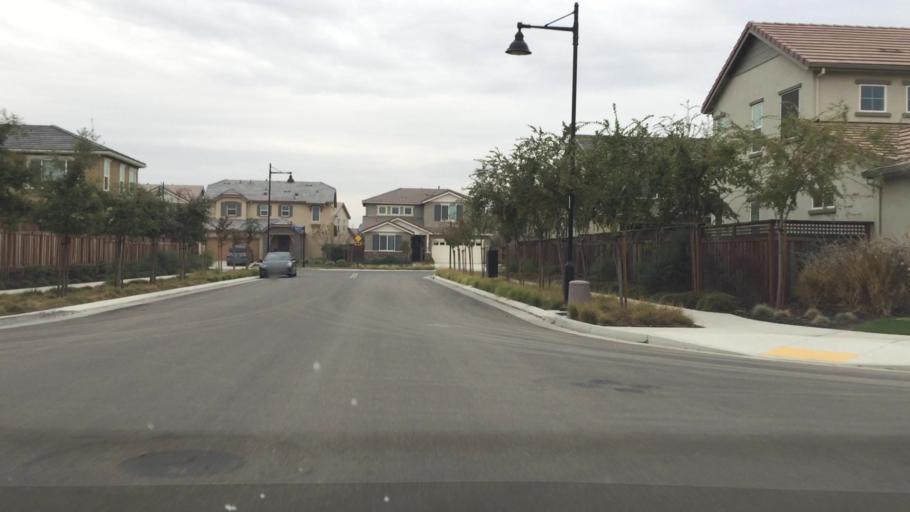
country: US
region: California
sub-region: San Joaquin County
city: Lathrop
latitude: 37.7937
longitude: -121.3192
